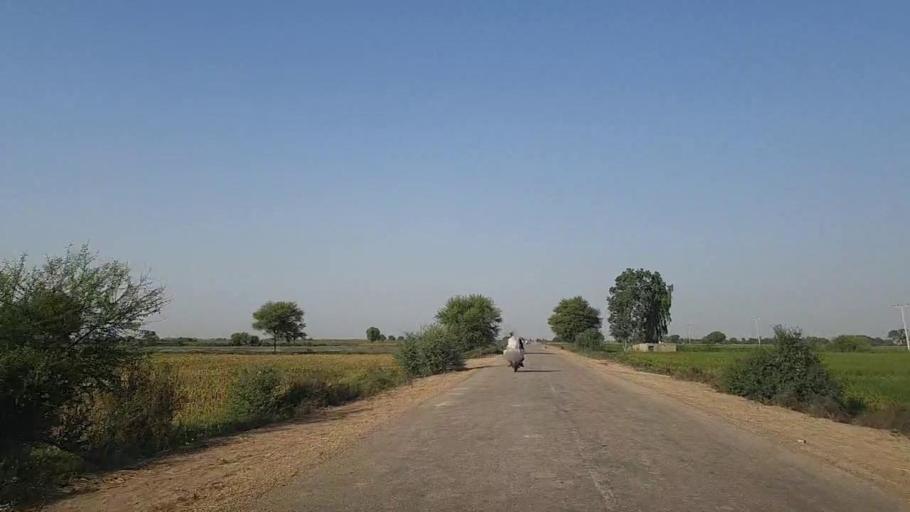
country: PK
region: Sindh
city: Mirpur Batoro
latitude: 24.5865
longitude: 68.3972
